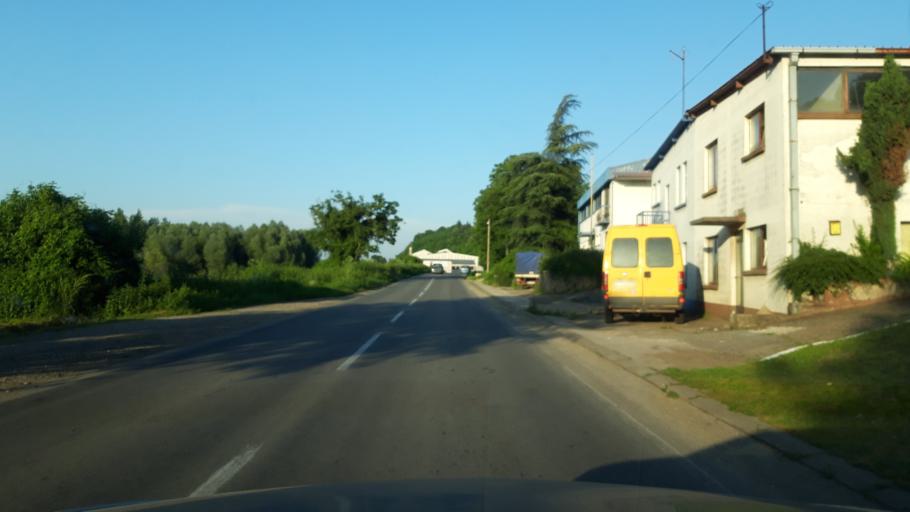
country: RS
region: Autonomna Pokrajina Vojvodina
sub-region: Juznobacki Okrug
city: Beocin
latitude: 45.2086
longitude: 19.7590
